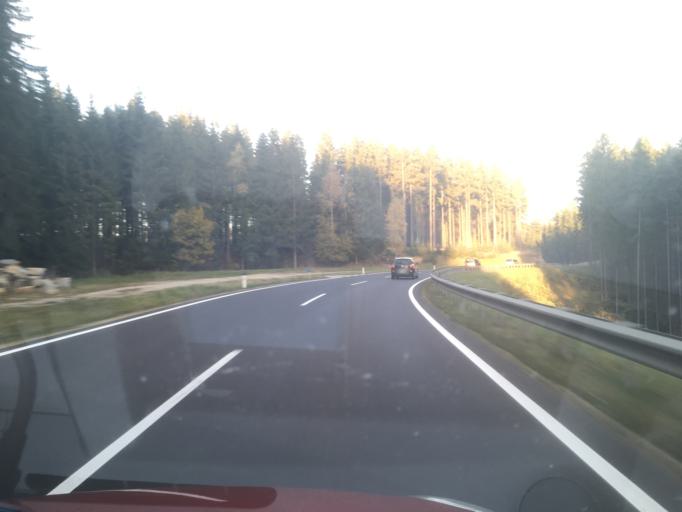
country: AT
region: Upper Austria
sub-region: Politischer Bezirk Freistadt
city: Freistadt
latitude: 48.5282
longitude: 14.5828
